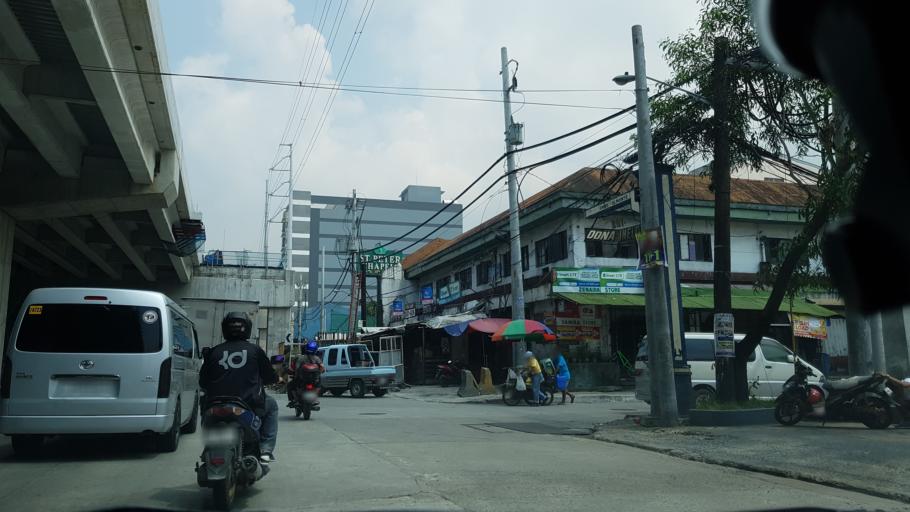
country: PH
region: Metro Manila
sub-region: San Juan
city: San Juan
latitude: 14.6113
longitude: 121.0171
